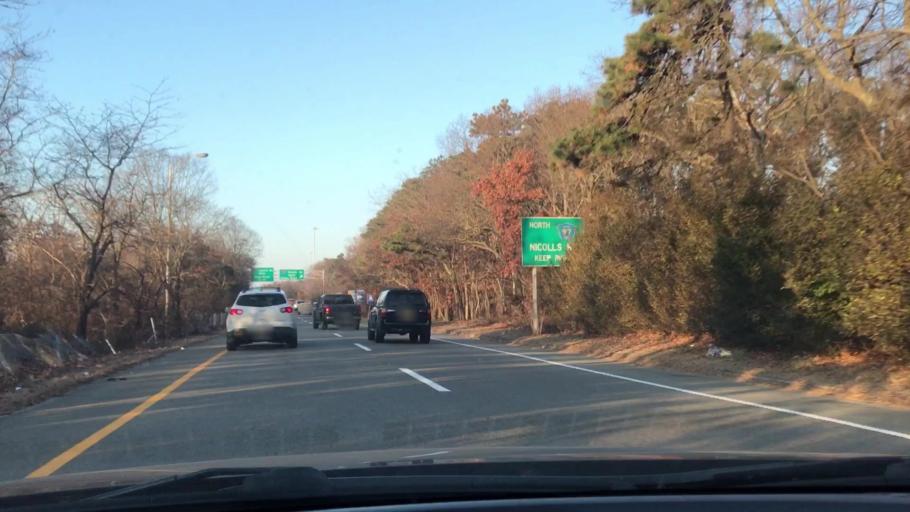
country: US
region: New York
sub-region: Suffolk County
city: Holtsville
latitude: 40.8213
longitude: -73.0494
